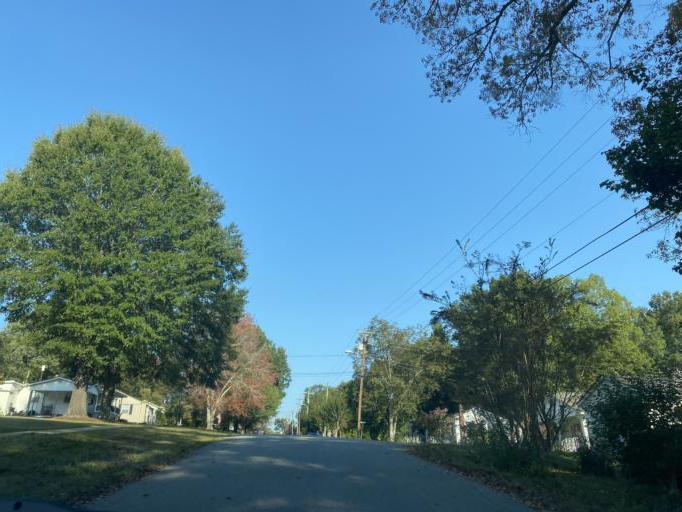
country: US
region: South Carolina
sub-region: Cherokee County
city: Gaffney
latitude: 35.0559
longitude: -81.6594
